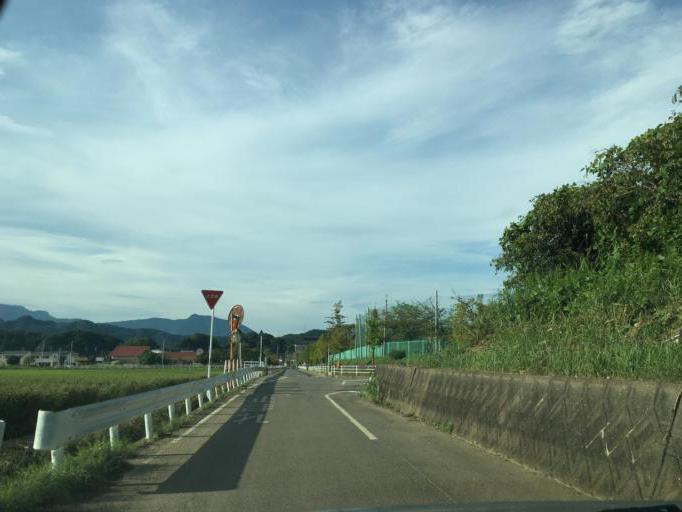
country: JP
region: Saga Prefecture
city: Takeocho-takeo
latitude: 33.2161
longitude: 130.0686
